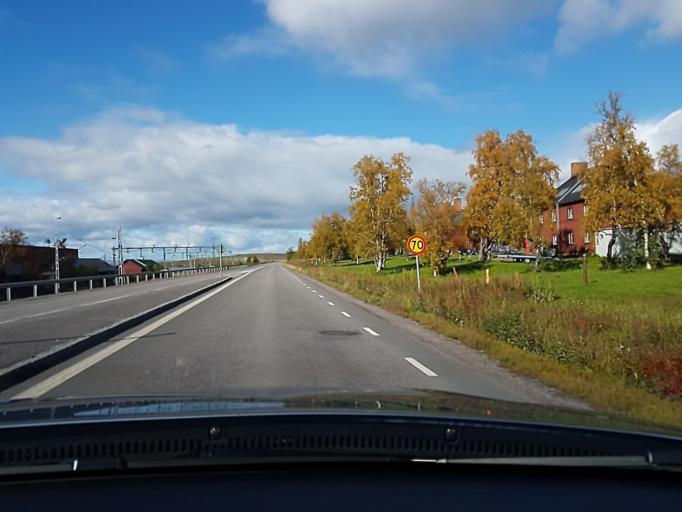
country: SE
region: Norrbotten
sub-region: Kiruna Kommun
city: Kiruna
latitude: 67.8599
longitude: 20.2100
